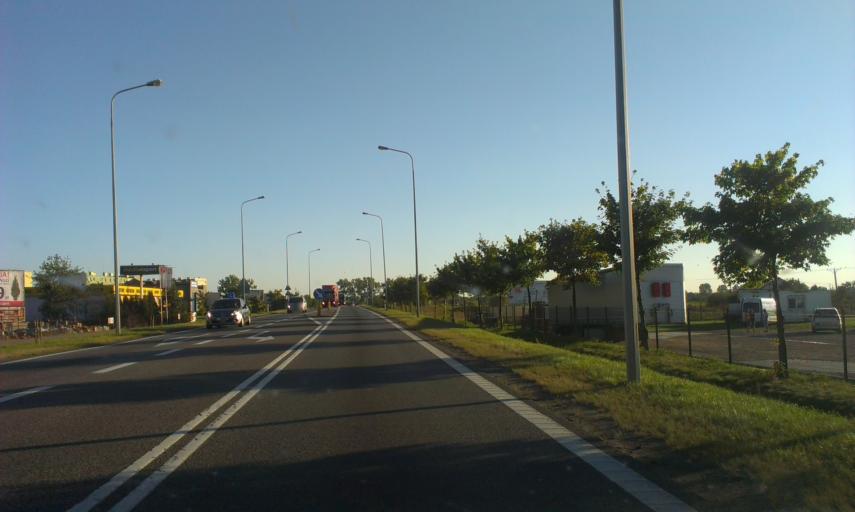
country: PL
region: Pomeranian Voivodeship
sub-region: Powiat czluchowski
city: Czluchow
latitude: 53.6635
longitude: 17.3468
